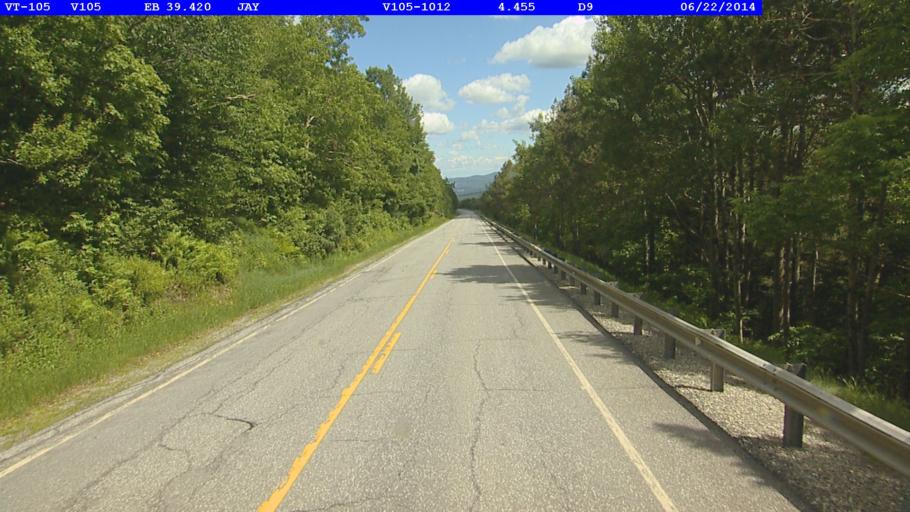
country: CA
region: Quebec
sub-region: Monteregie
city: Sutton
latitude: 44.9851
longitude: -72.4938
